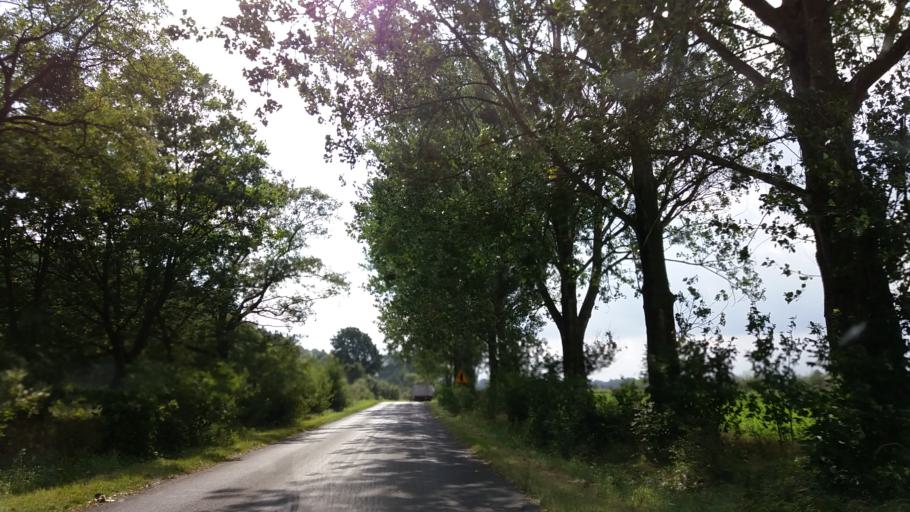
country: PL
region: West Pomeranian Voivodeship
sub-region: Powiat choszczenski
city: Choszczno
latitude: 53.1361
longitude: 15.4546
